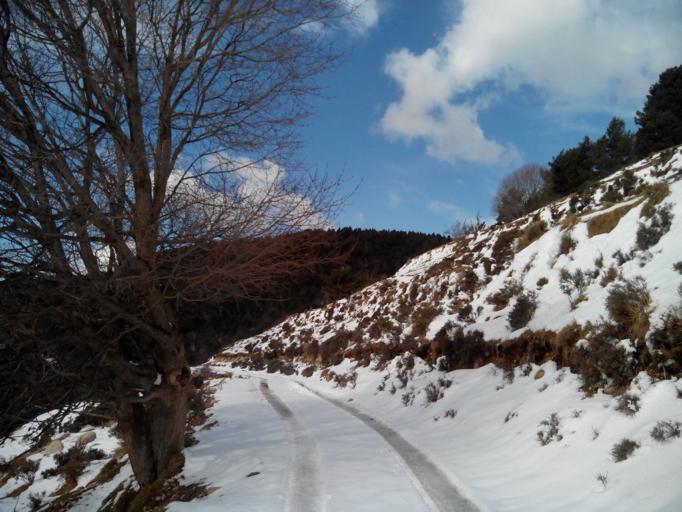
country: ES
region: Catalonia
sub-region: Provincia de Barcelona
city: Sant Julia de Cerdanyola
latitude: 42.1967
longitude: 1.9444
